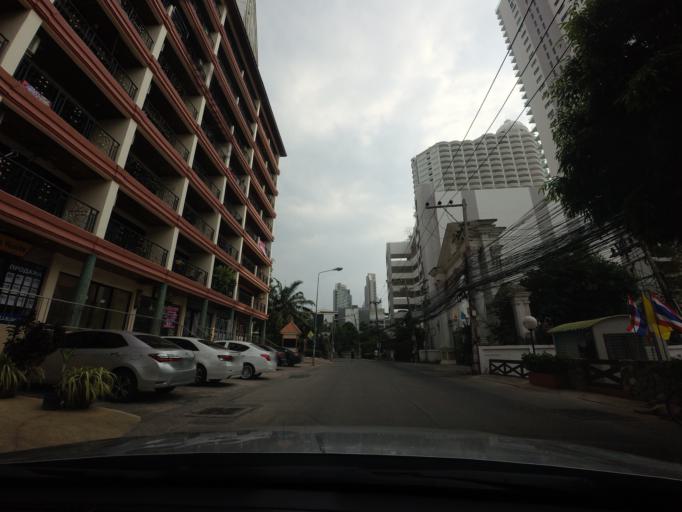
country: TH
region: Chon Buri
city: Phatthaya
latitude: 12.9681
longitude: 100.8849
